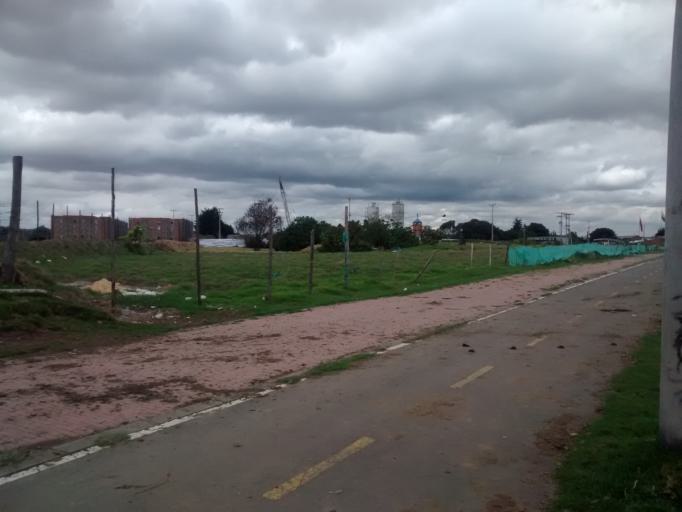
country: CO
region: Cundinamarca
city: Cota
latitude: 4.7222
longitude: -74.1046
